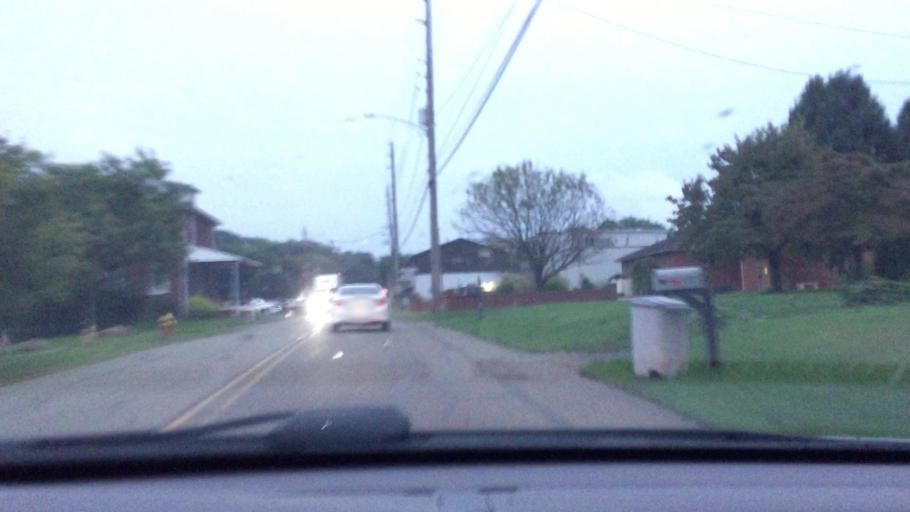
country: US
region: Pennsylvania
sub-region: Allegheny County
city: Cheswick
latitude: 40.5564
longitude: -79.8214
